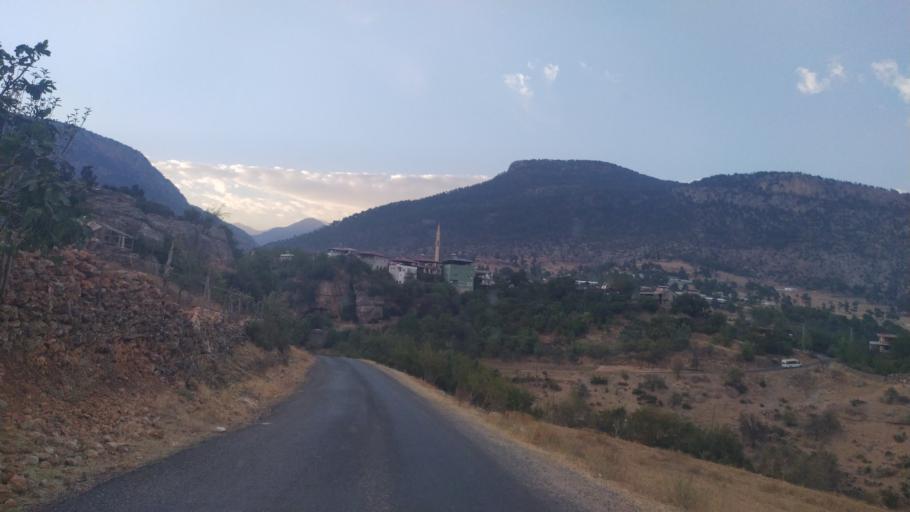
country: TR
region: Mersin
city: Camliyayla
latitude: 37.2365
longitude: 34.7177
